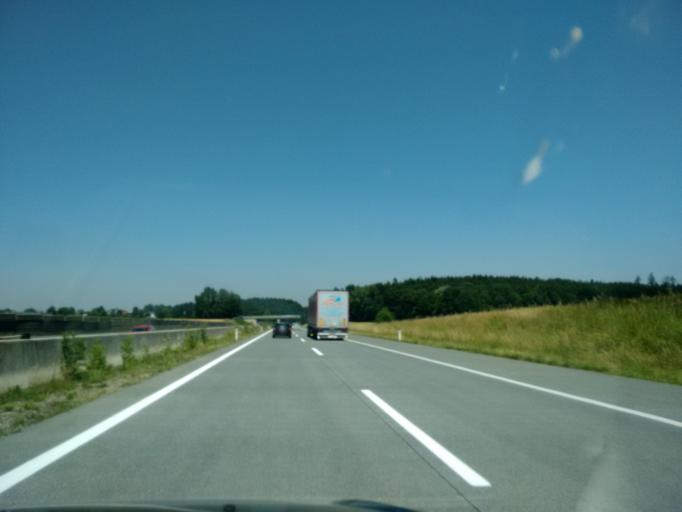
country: AT
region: Upper Austria
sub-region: Politischer Bezirk Vocklabruck
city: Desselbrunn
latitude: 47.9838
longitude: 13.7758
